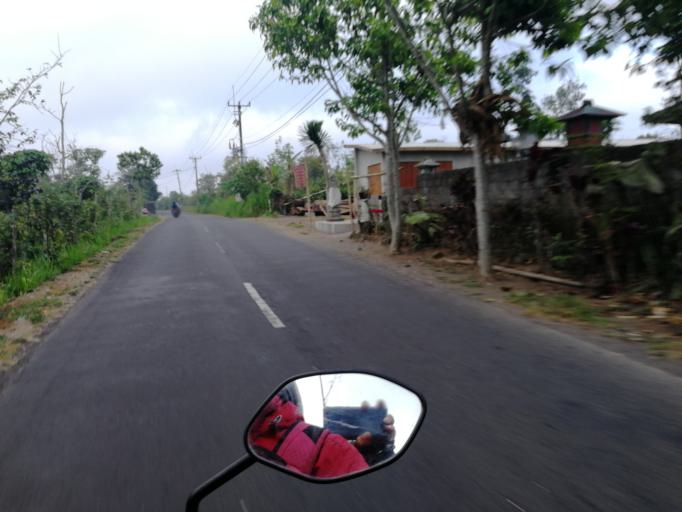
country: ID
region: Bali
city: Banjar Ambengan
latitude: -8.2325
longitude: 115.2422
